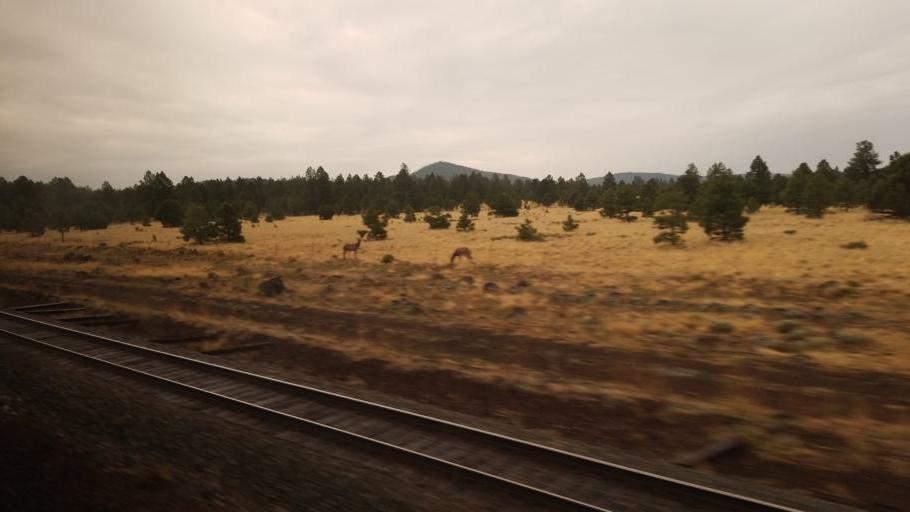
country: US
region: Arizona
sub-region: Coconino County
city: Parks
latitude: 35.2512
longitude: -111.9499
